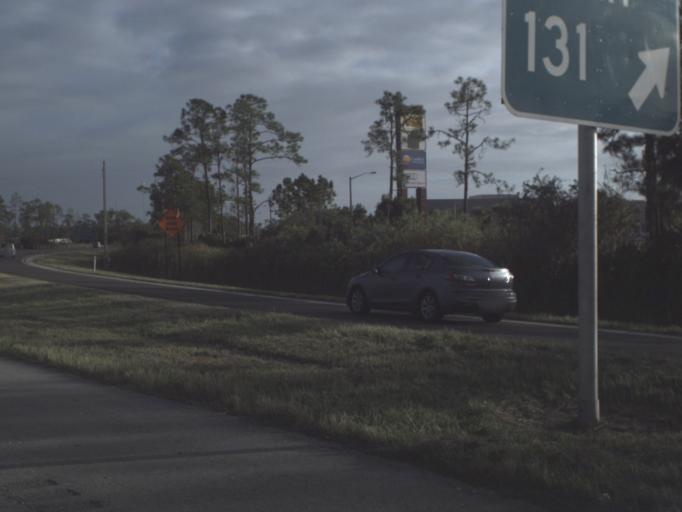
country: US
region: Florida
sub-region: Lee County
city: Gateway
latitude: 26.5429
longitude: -81.7948
